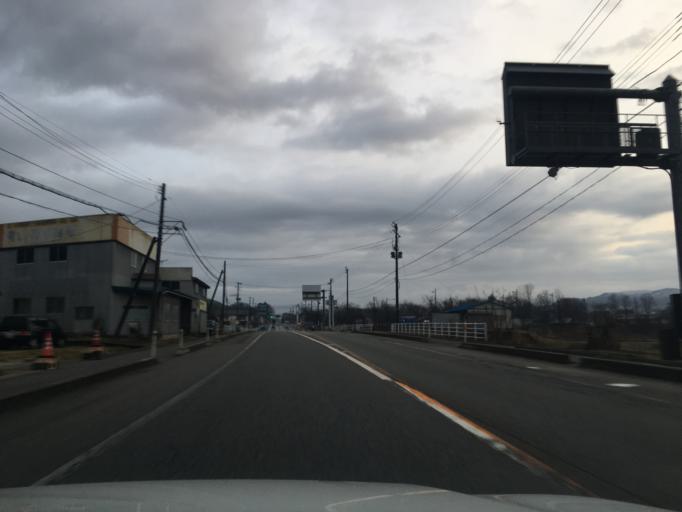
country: JP
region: Niigata
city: Murakami
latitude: 38.2804
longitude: 139.5205
